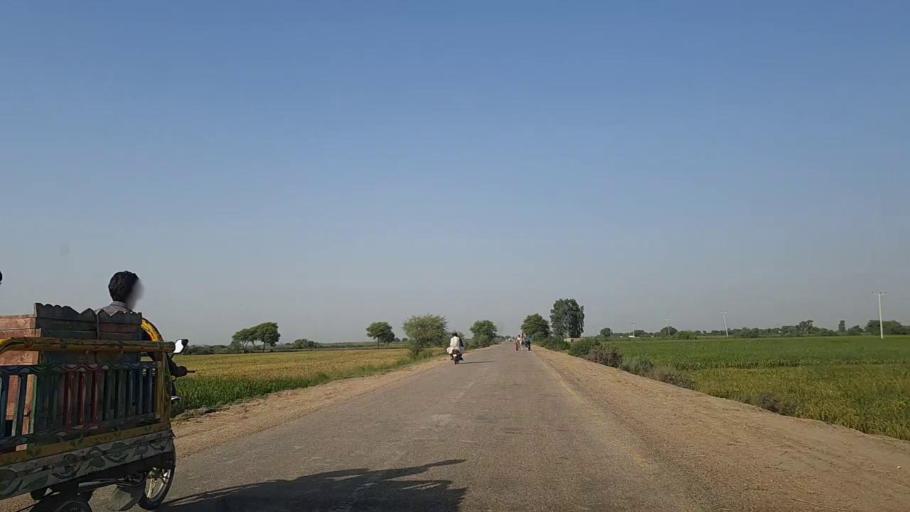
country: PK
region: Sindh
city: Mirpur Batoro
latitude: 24.5857
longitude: 68.3970
